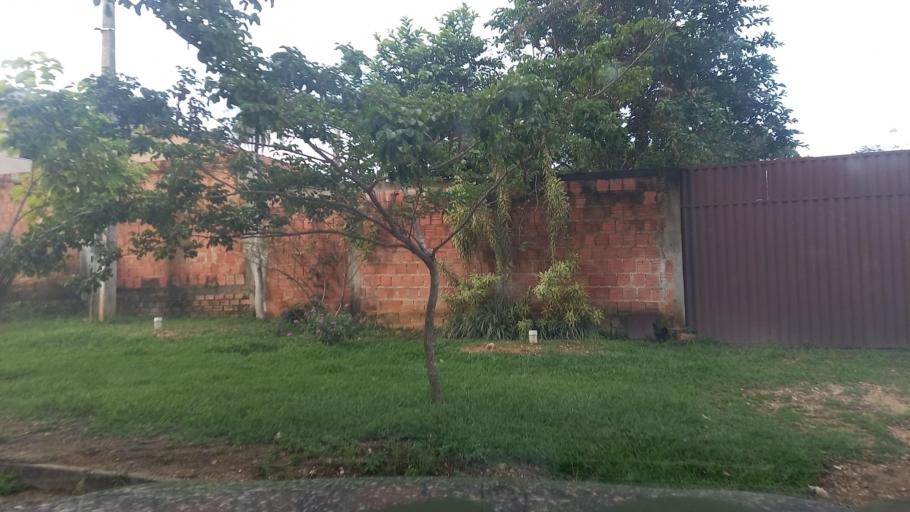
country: BR
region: Goias
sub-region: Cavalcante
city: Cavalcante
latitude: -13.7939
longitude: -47.4535
